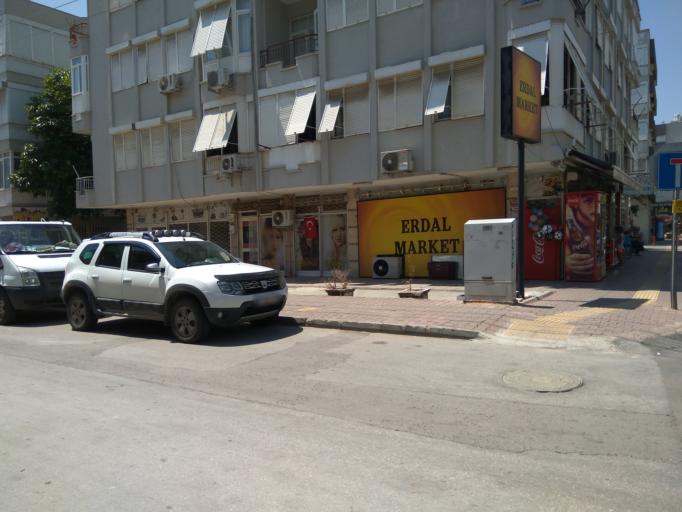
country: TR
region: Antalya
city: Antalya
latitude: 36.8988
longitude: 30.6963
